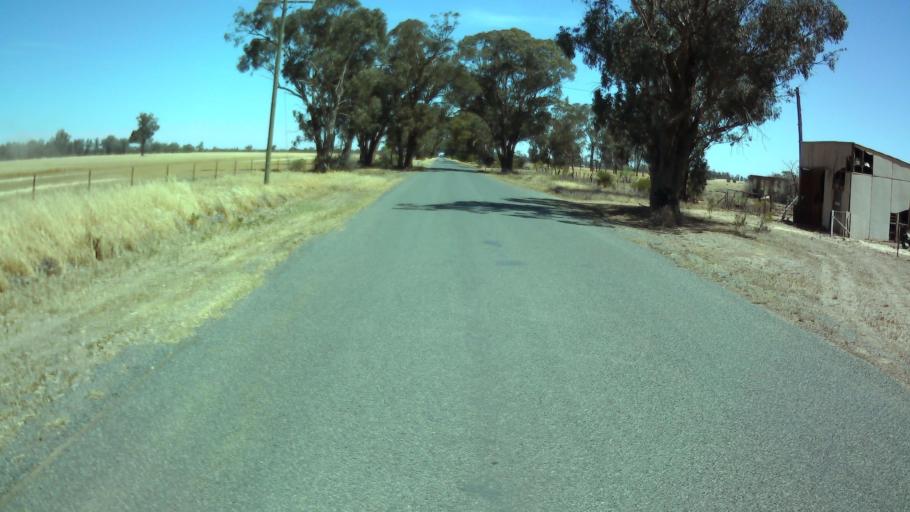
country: AU
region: New South Wales
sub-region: Weddin
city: Grenfell
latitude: -34.0160
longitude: 147.7936
